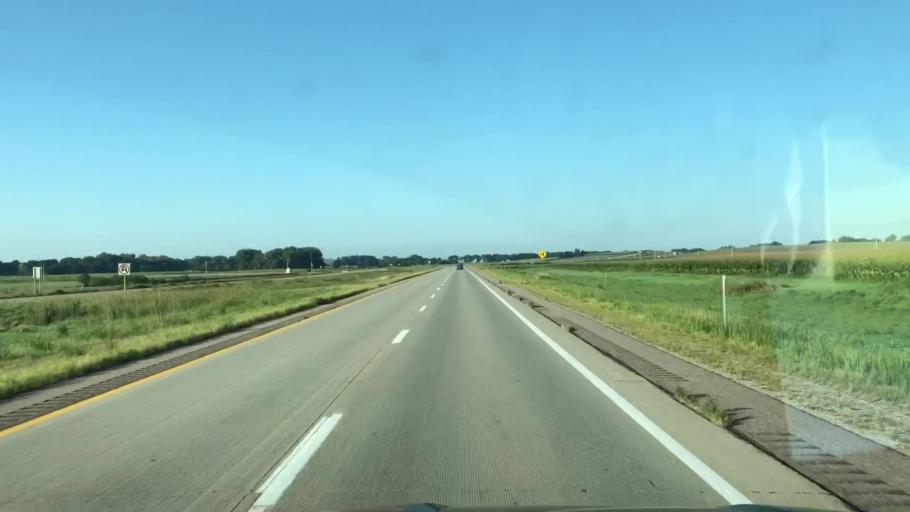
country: US
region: Iowa
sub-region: Plymouth County
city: Le Mars
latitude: 42.8699
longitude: -96.1119
